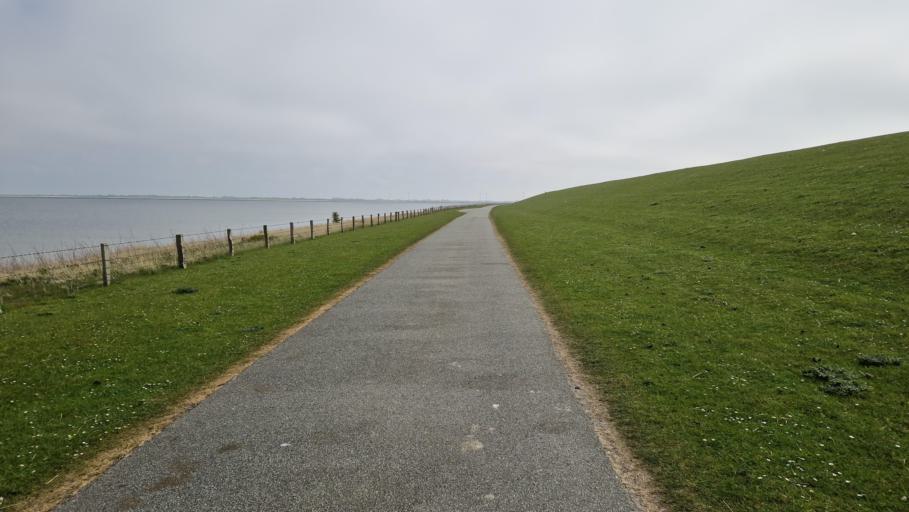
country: DE
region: Schleswig-Holstein
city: Elisabeth-Sophien-Koog
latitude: 54.5492
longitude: 8.8783
